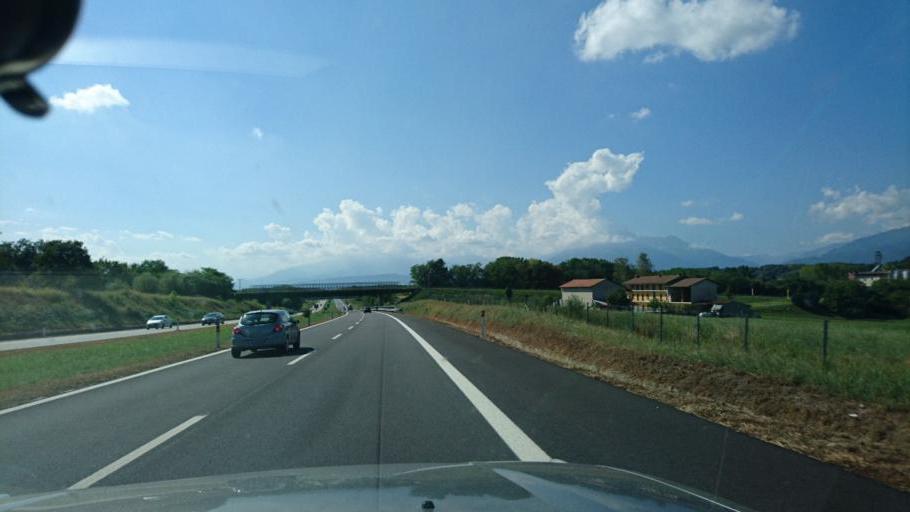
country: IT
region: Piedmont
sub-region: Provincia di Torino
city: Settimo Rottaro
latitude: 45.4149
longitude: 7.9950
